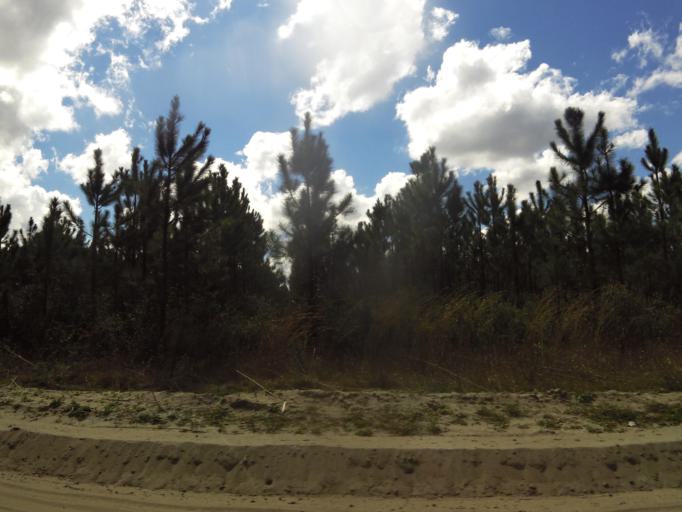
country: US
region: Florida
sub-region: Clay County
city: Green Cove Springs
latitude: 29.8365
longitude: -81.8086
